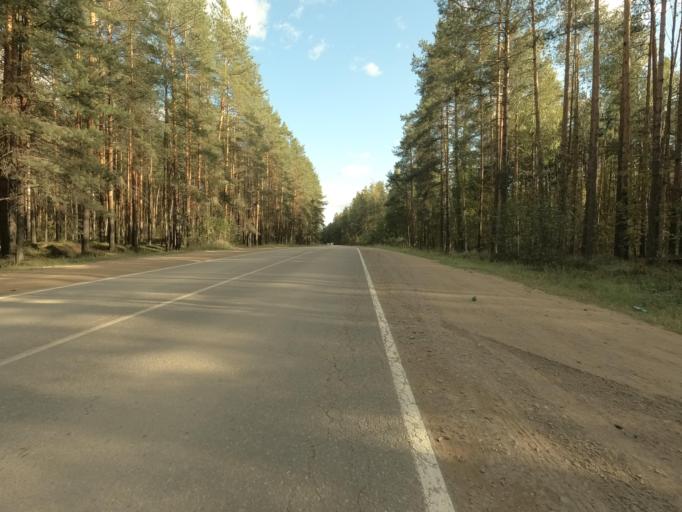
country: RU
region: Leningrad
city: Imeni Sverdlova
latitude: 59.8429
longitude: 30.6900
